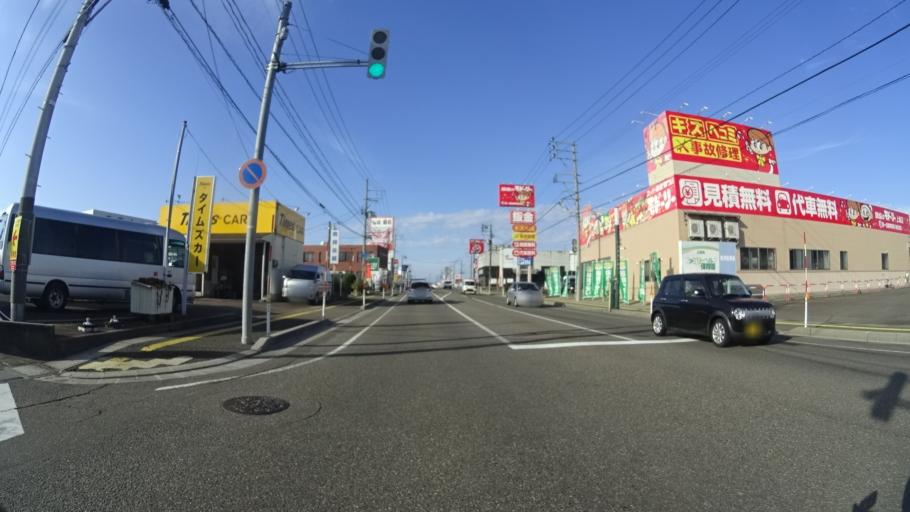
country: JP
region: Niigata
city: Joetsu
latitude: 37.1328
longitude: 138.2439
